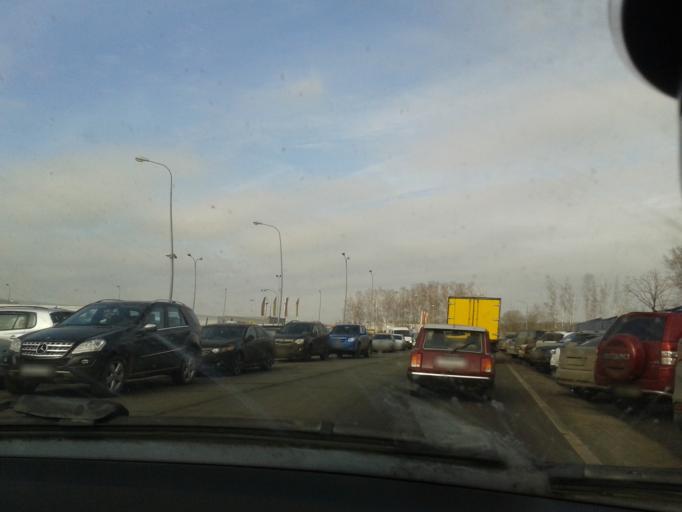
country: RU
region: Moscow
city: Lianozovo
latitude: 55.9151
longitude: 37.5903
